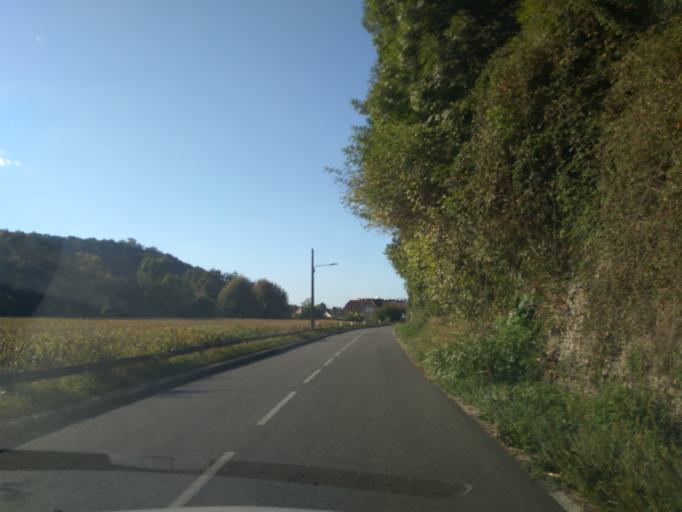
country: FR
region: Aquitaine
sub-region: Departement des Pyrenees-Atlantiques
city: Gelos
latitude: 43.2746
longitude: -0.3720
